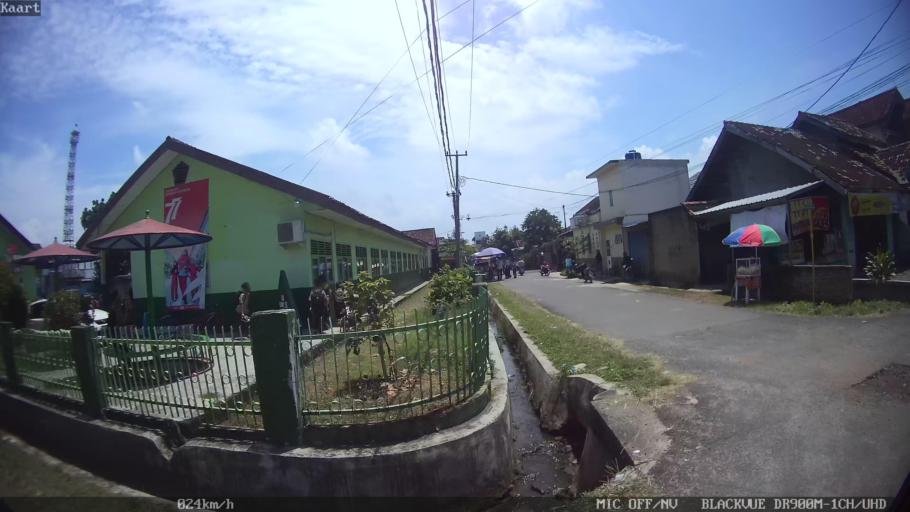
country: ID
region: Lampung
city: Kedaton
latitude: -5.3624
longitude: 105.2855
